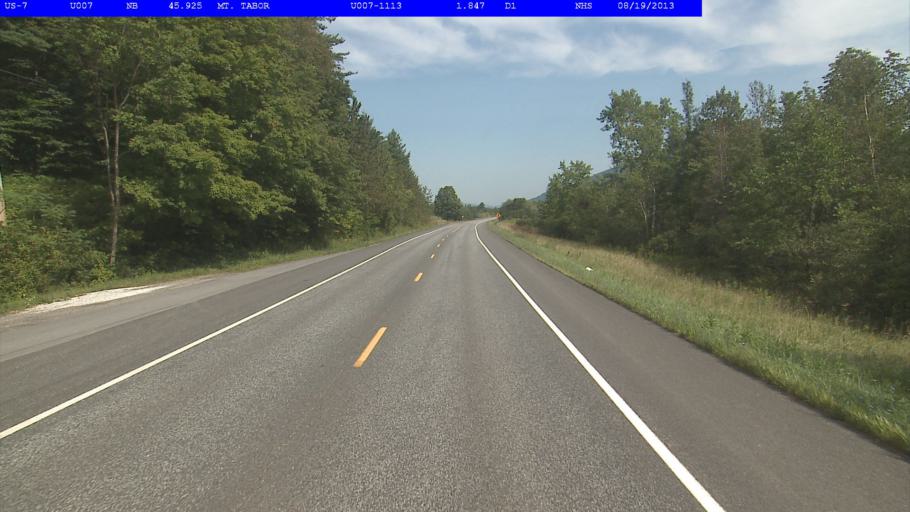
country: US
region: Vermont
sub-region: Bennington County
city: Manchester Center
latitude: 43.3315
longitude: -72.9921
